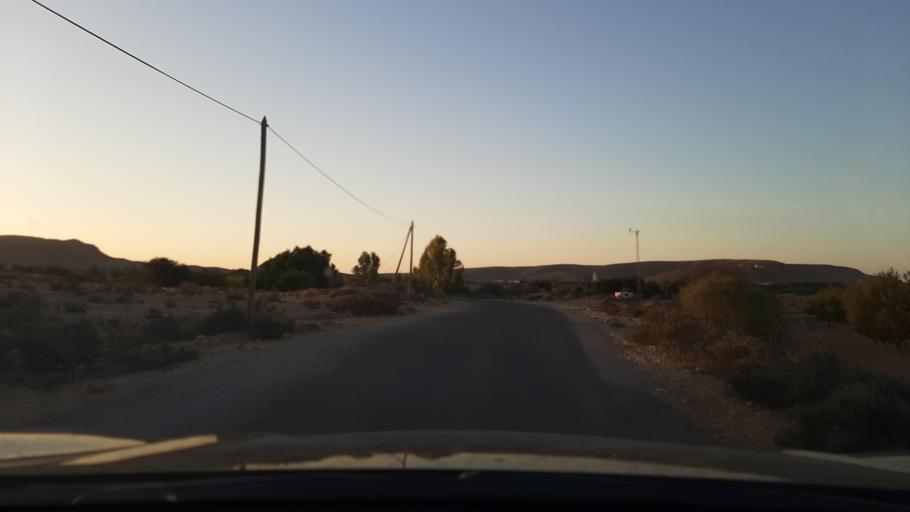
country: TN
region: Qabis
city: Matmata
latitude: 33.5621
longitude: 10.1812
